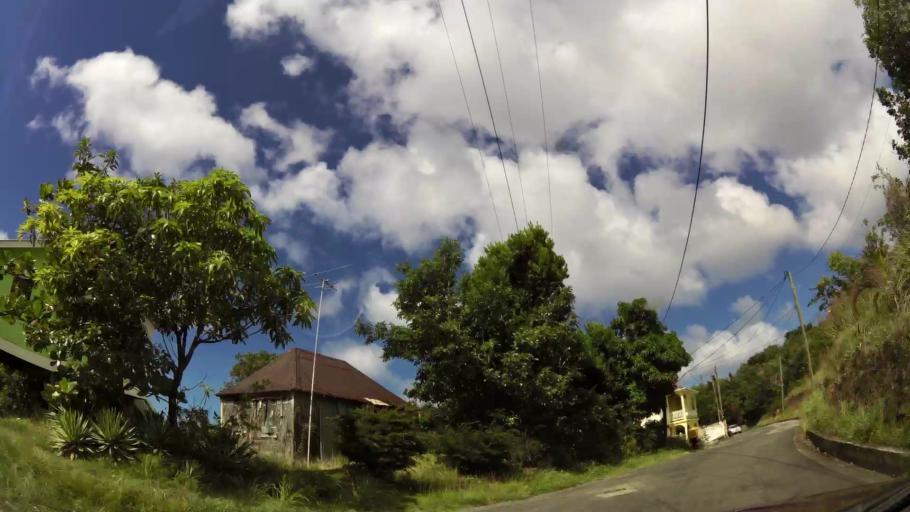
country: DM
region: Saint John
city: Portsmouth
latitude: 15.6059
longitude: -61.4634
